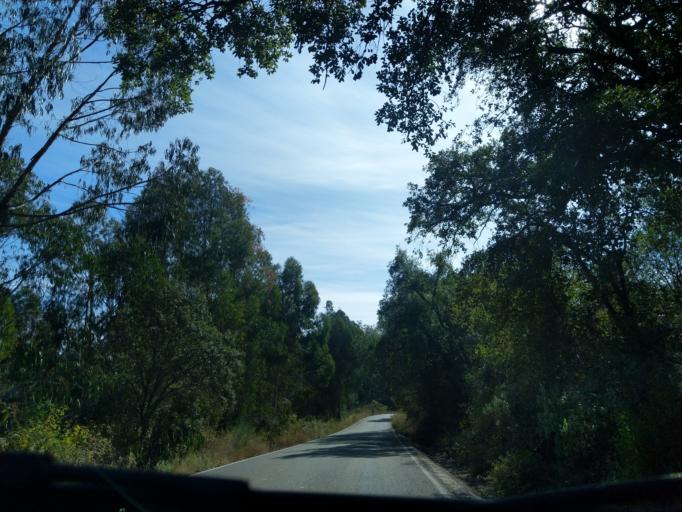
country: ES
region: Extremadura
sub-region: Provincia de Badajoz
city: Reina
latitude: 38.1250
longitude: -5.9128
